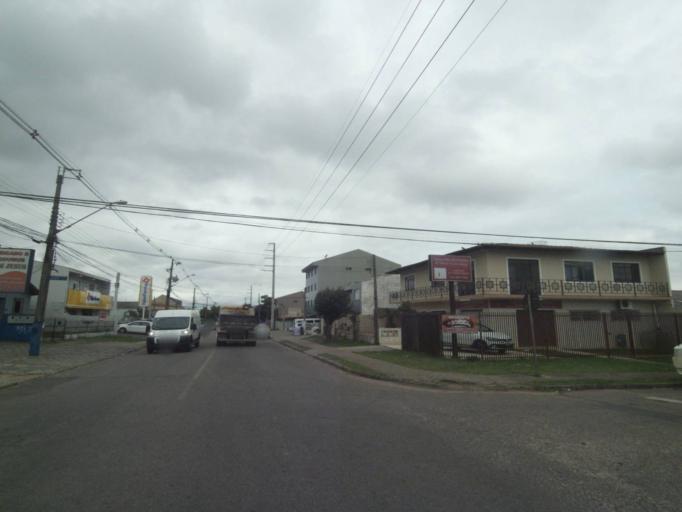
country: BR
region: Parana
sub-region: Sao Jose Dos Pinhais
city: Sao Jose dos Pinhais
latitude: -25.5441
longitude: -49.2811
